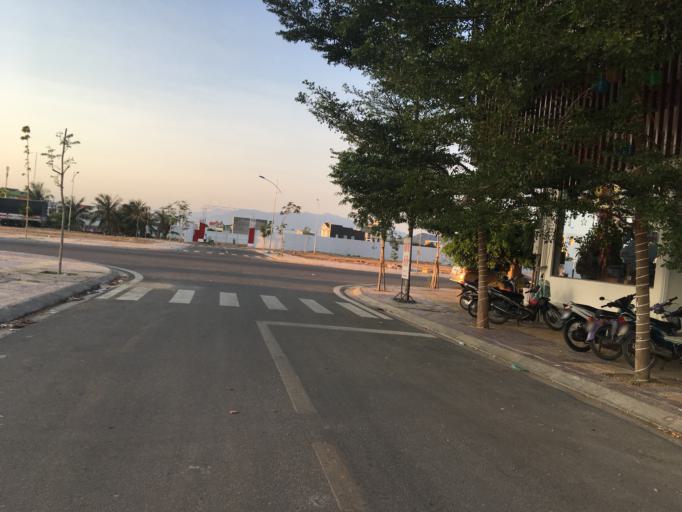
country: VN
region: Ninh Thuan
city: Phan Rang-Thap Cham
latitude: 11.5700
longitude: 108.9963
